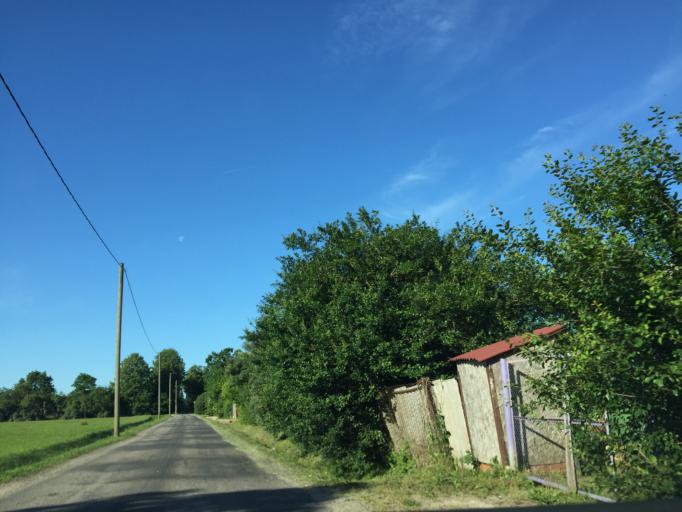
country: LV
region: Ventspils
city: Ventspils
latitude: 57.3675
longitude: 21.6072
